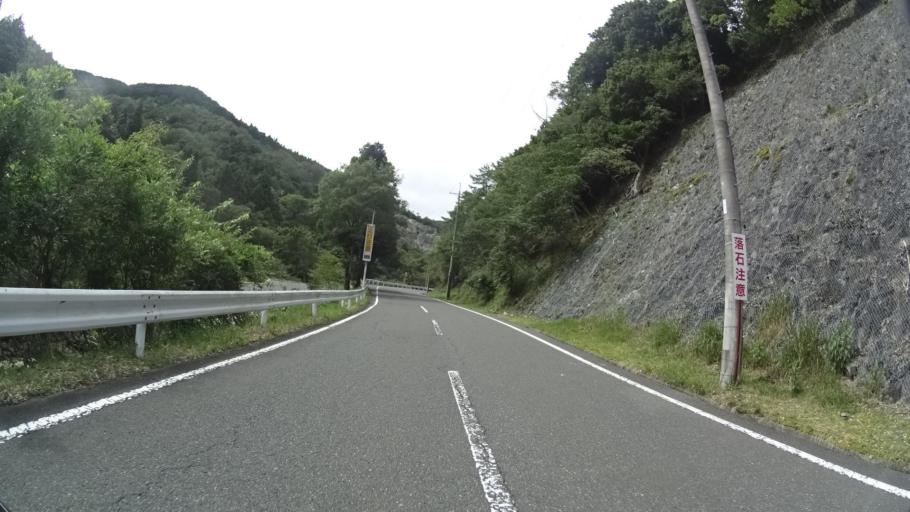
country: JP
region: Kyoto
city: Miyazu
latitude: 35.4670
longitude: 135.1515
